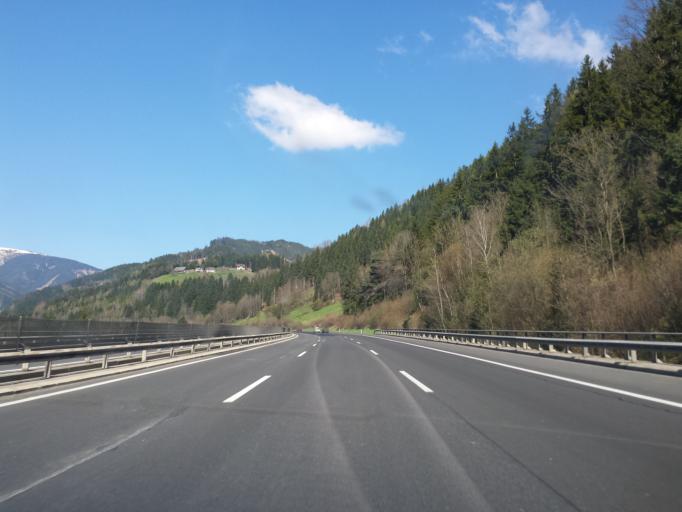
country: AT
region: Styria
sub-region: Politischer Bezirk Graz-Umgebung
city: Ubelbach
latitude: 47.2409
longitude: 15.1969
